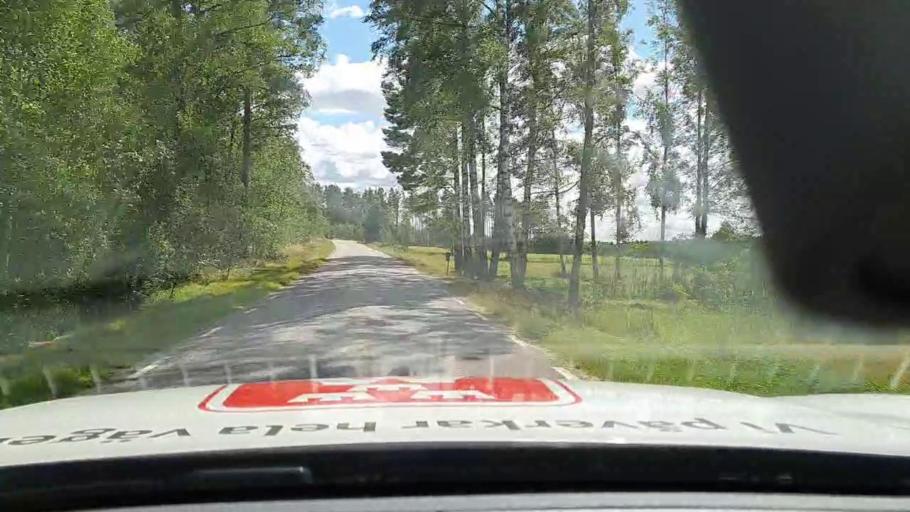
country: SE
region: Vaestra Goetaland
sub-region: Toreboda Kommun
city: Toereboda
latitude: 58.5827
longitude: 14.1220
